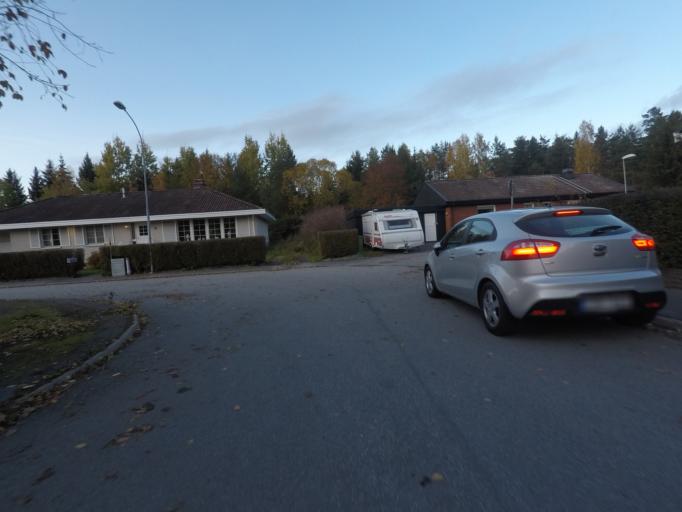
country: SE
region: OErebro
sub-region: Karlskoga Kommun
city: Karlskoga
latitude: 59.3105
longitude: 14.4710
